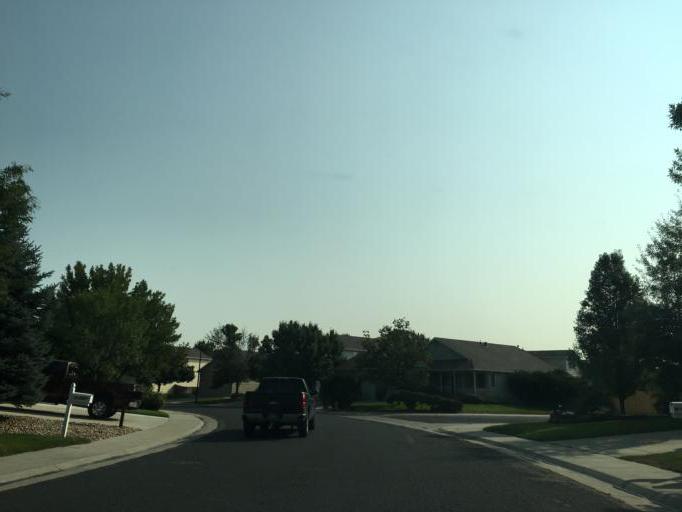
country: US
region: Colorado
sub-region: Adams County
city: Todd Creek
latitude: 39.9073
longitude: -104.8531
